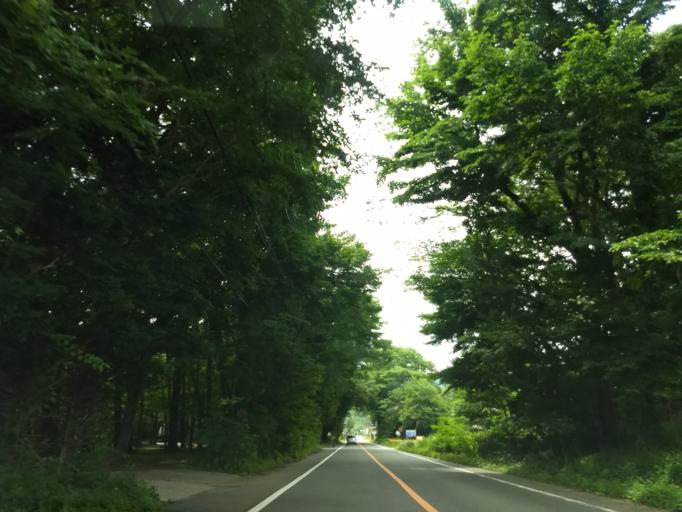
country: JP
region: Shizuoka
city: Gotemba
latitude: 35.4229
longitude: 138.9041
